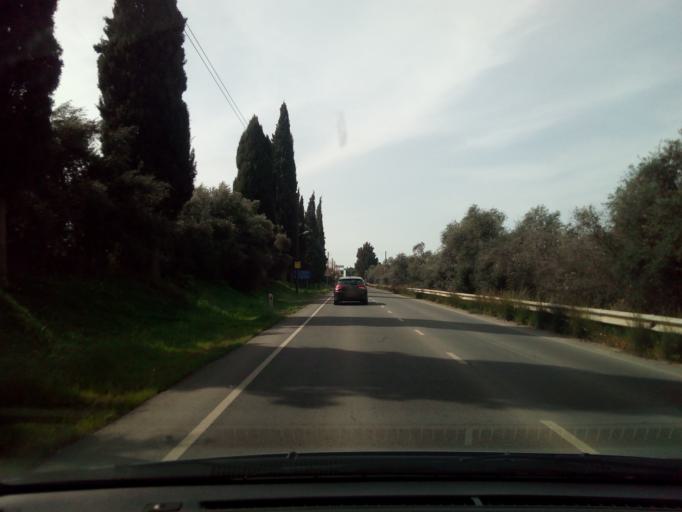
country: CY
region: Lefkosia
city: Kato Deftera
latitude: 35.0915
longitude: 33.2889
